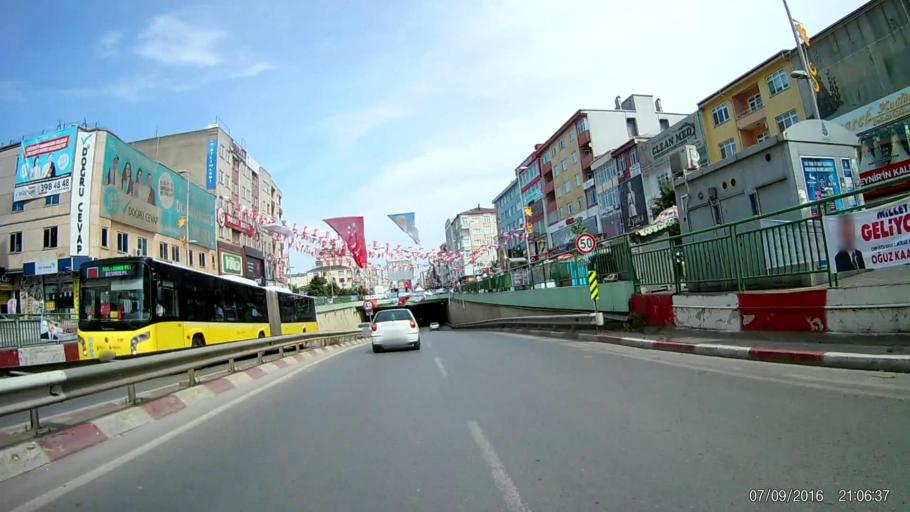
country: TR
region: Istanbul
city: Sultanbeyli
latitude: 40.9681
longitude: 29.2635
